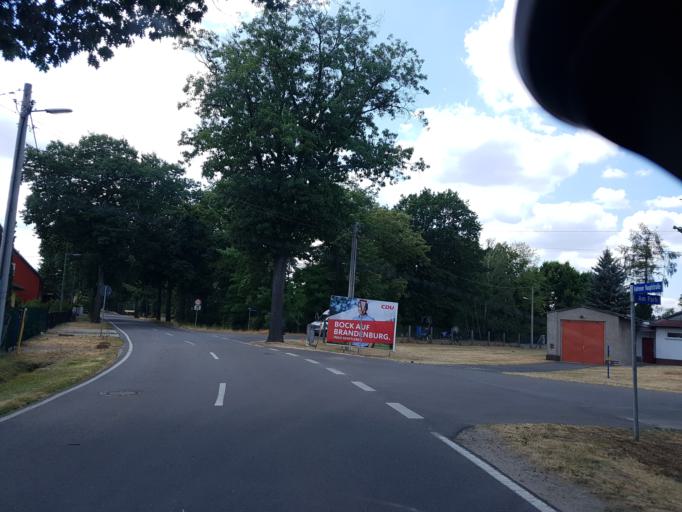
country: DE
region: Brandenburg
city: Cottbus
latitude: 51.7216
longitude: 14.4089
